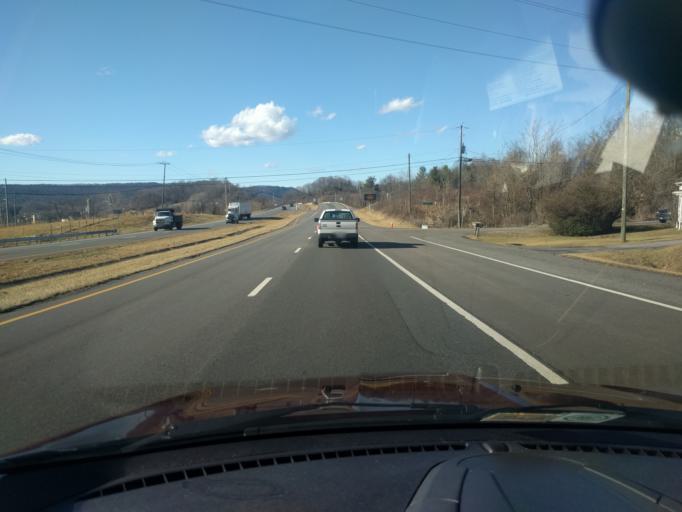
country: US
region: Virginia
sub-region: Botetourt County
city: Cloverdale
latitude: 37.3817
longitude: -79.8930
